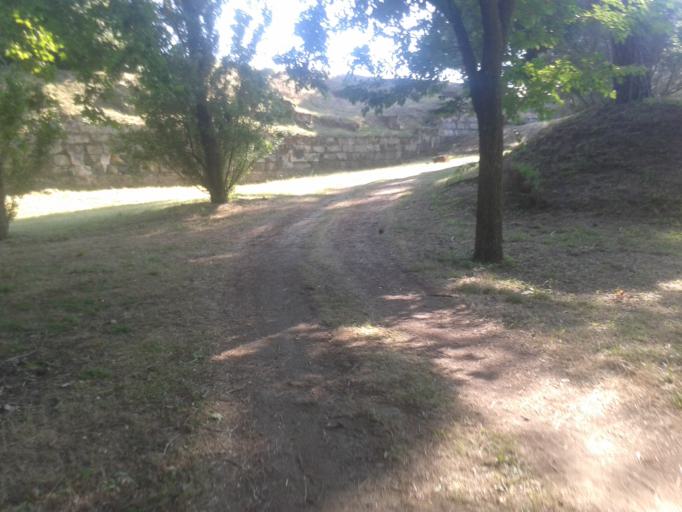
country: IT
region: Campania
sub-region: Provincia di Napoli
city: Pompei
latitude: 40.7542
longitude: 14.4896
